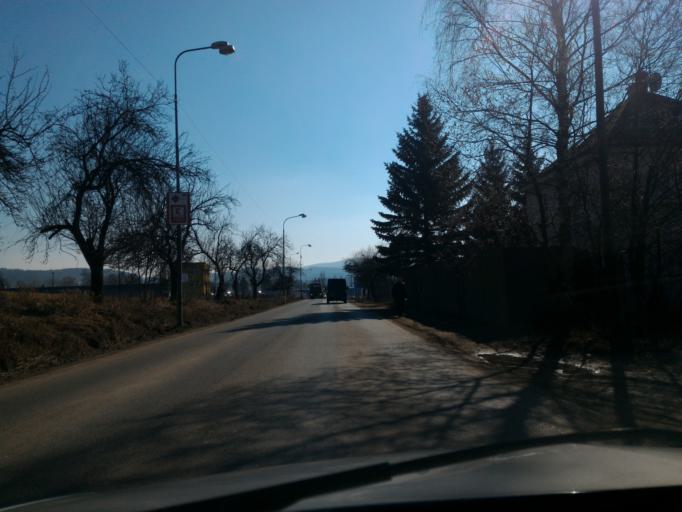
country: CZ
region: Liberecky
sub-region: Okres Jablonec nad Nisou
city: Jablonec nad Nisou
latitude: 50.7442
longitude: 15.1448
